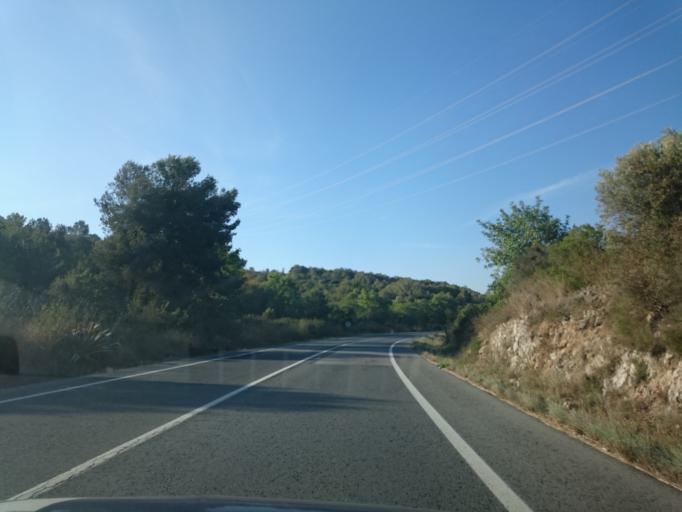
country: ES
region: Catalonia
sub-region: Provincia de Barcelona
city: Vilanova i la Geltru
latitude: 41.2577
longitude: 1.7160
